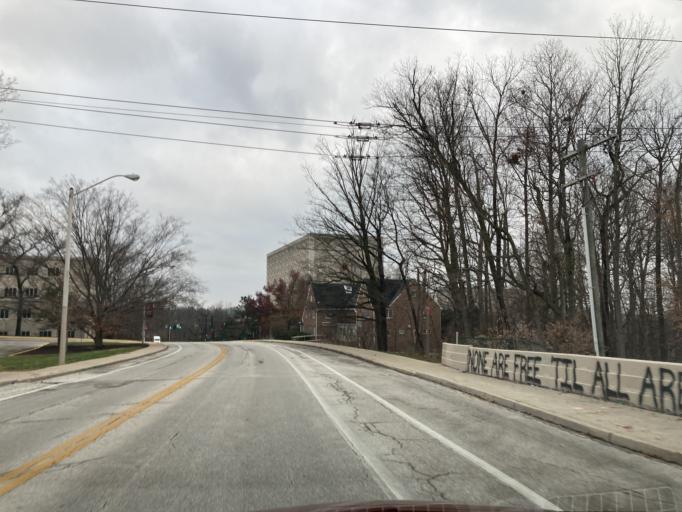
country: US
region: Indiana
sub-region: Monroe County
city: Bloomington
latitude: 39.1732
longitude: -86.5156
